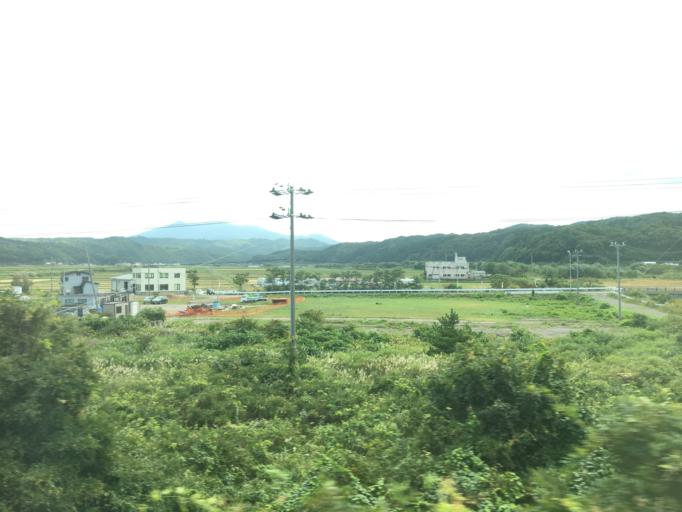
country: JP
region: Aomori
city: Shimokizukuri
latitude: 40.7599
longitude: 140.1593
